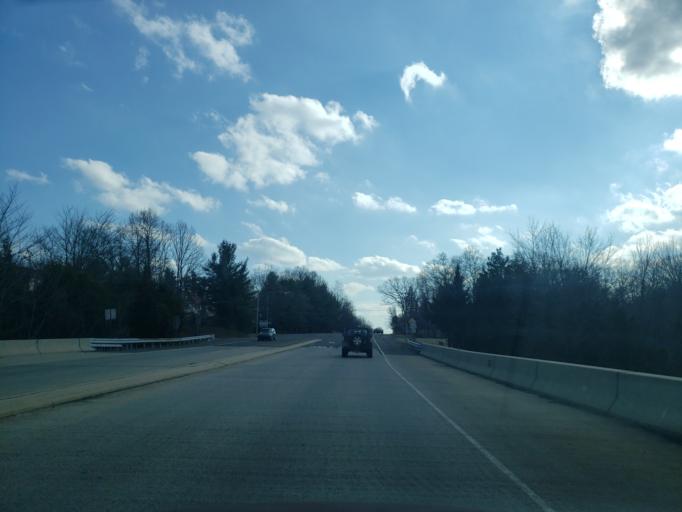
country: US
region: Pennsylvania
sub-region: Bucks County
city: Doylestown
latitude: 40.2989
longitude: -75.1281
